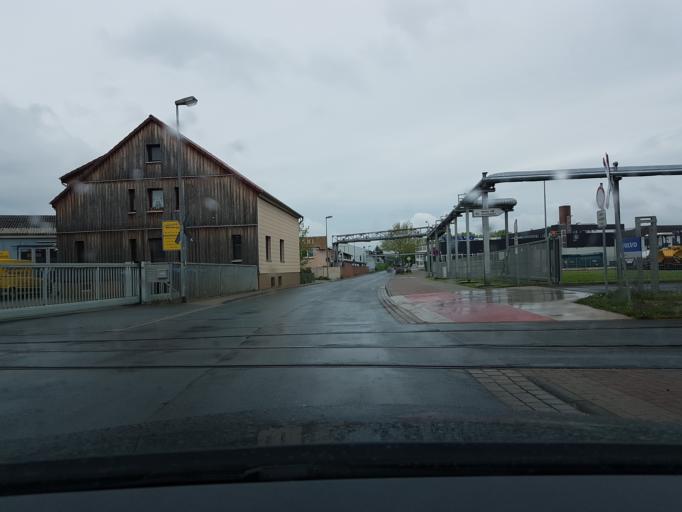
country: DE
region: Lower Saxony
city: Hameln
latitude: 52.0952
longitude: 9.3669
